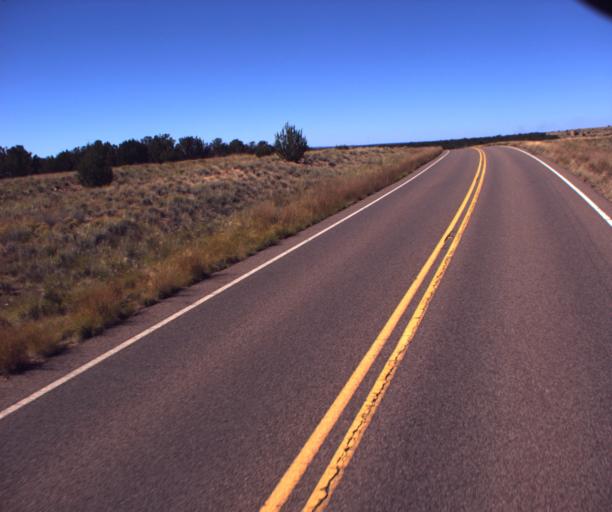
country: US
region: Arizona
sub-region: Navajo County
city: Taylor
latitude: 34.4829
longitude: -110.3317
